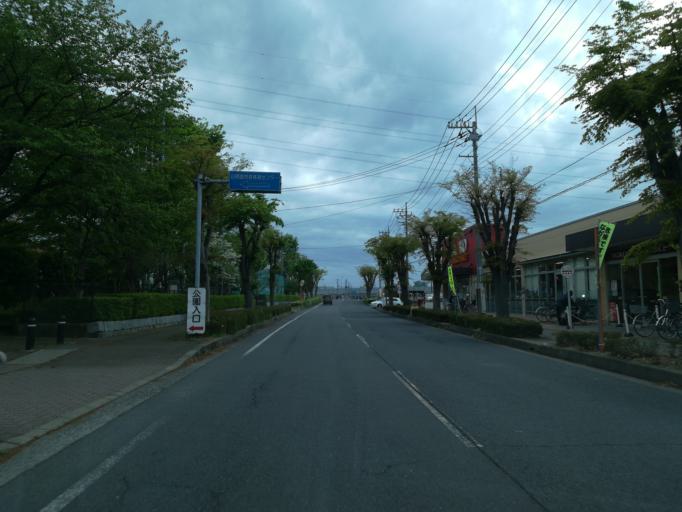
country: JP
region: Saitama
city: Shiraoka
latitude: 36.0320
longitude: 139.6730
